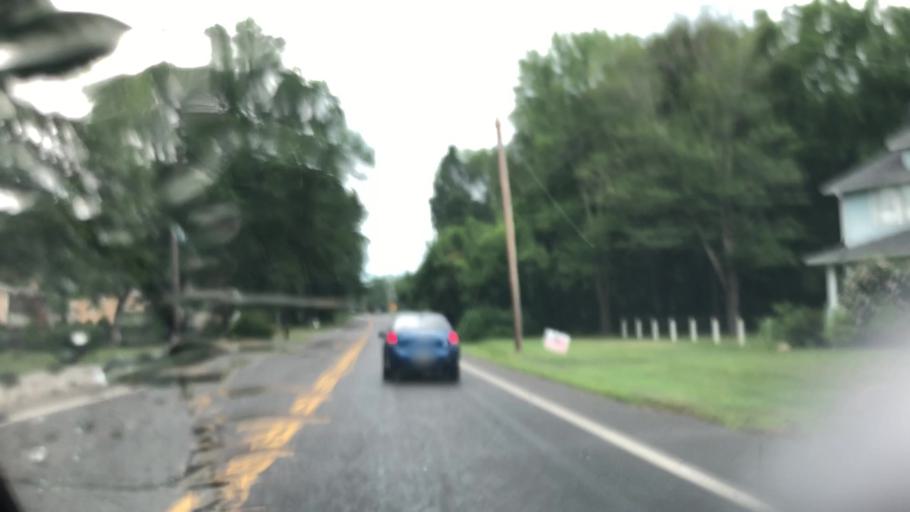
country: US
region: Ohio
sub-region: Stark County
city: Massillon
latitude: 40.8427
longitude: -81.4995
